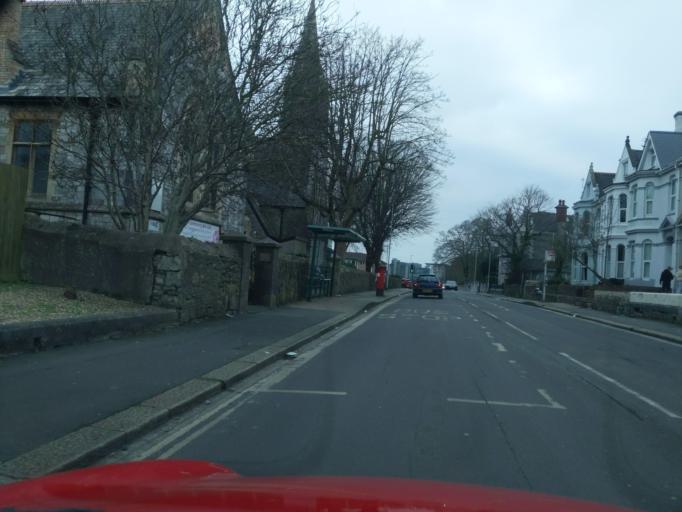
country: GB
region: England
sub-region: Plymouth
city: Plymouth
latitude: 50.3732
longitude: -4.1269
